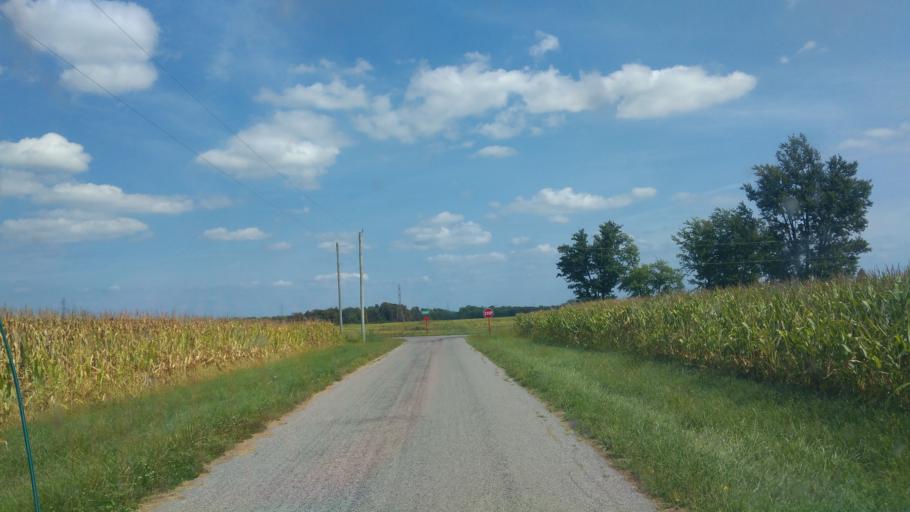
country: US
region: Ohio
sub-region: Union County
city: Richwood
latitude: 40.3957
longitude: -83.4287
